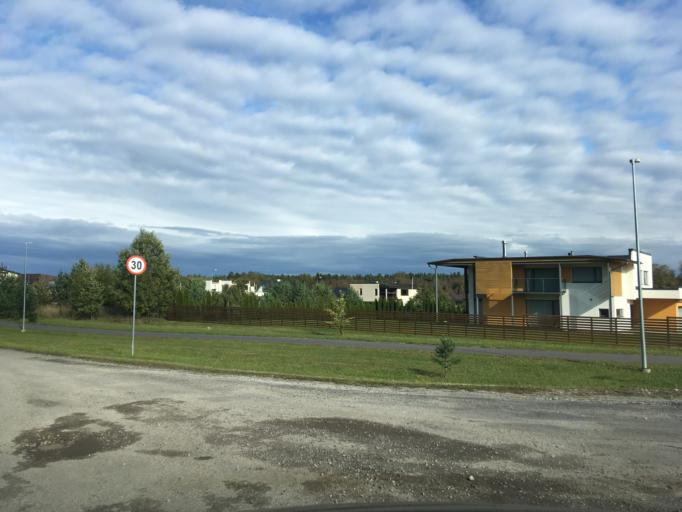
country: EE
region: Harju
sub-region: Saue vald
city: Laagri
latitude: 59.3417
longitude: 24.6496
